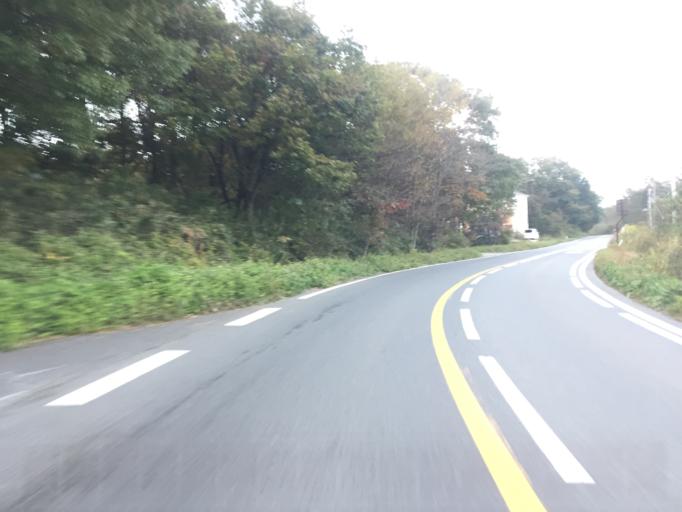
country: JP
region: Fukushima
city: Nihommatsu
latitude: 37.6275
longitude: 140.3504
